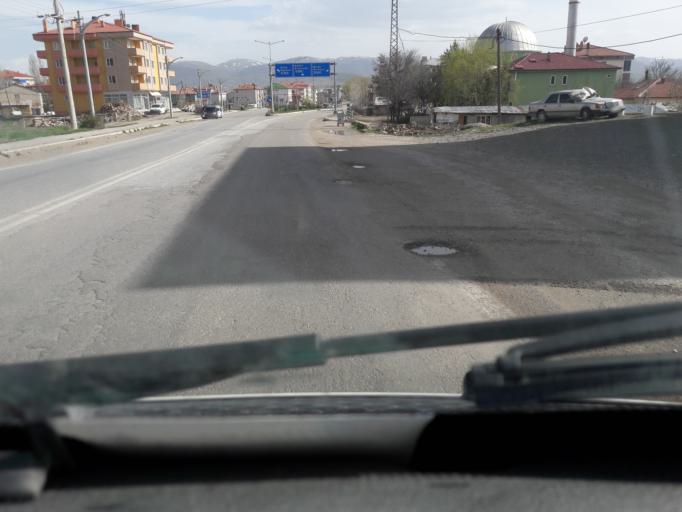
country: TR
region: Gumushane
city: Kelkit
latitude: 40.1448
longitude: 39.4329
